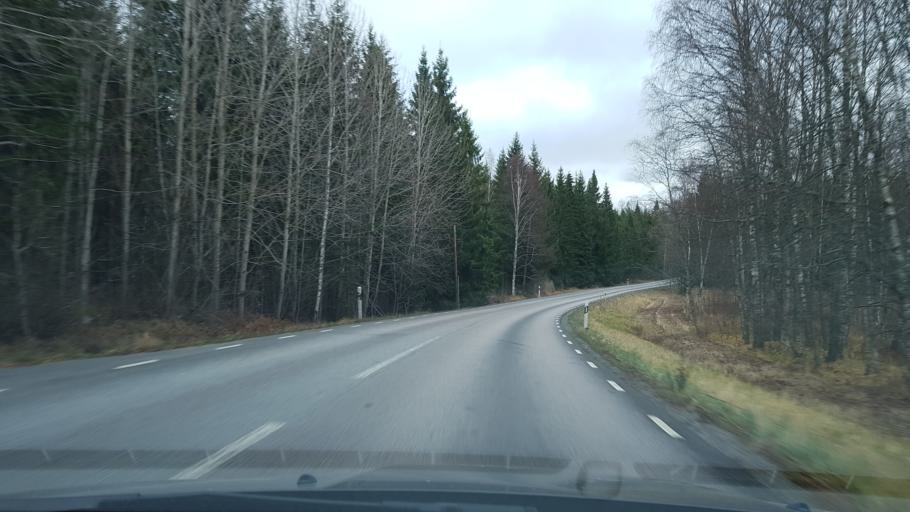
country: SE
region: Stockholm
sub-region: Norrtalje Kommun
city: Skanninge
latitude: 60.0390
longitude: 18.4936
